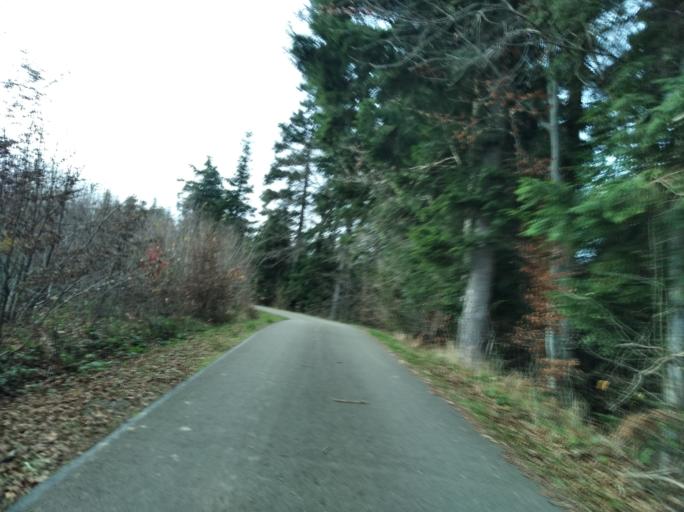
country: PL
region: Subcarpathian Voivodeship
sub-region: Powiat brzozowski
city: Domaradz
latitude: 49.7819
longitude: 21.9193
